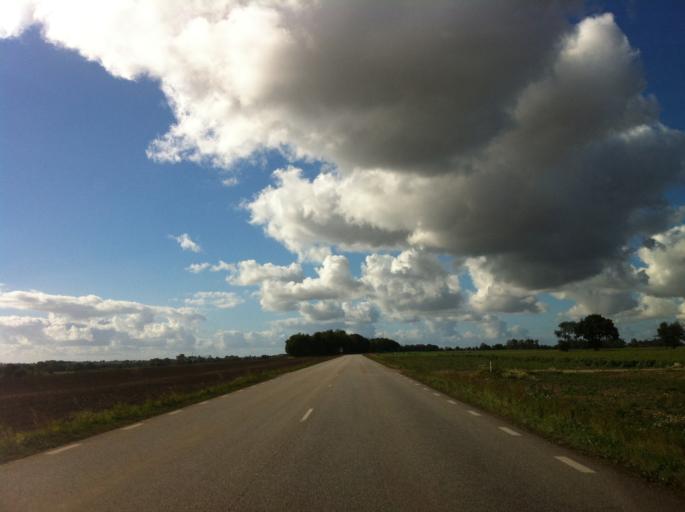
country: SE
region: Skane
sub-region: Eslovs Kommun
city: Eslov
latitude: 55.7889
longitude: 13.2412
